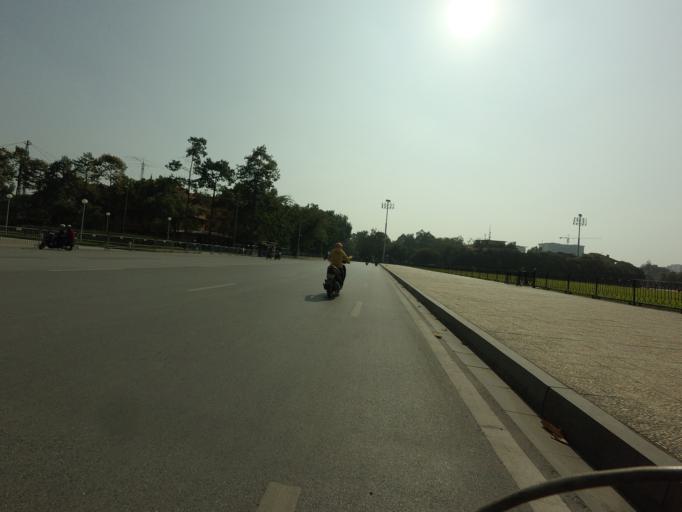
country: VN
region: Ha Noi
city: Hanoi
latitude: 21.0367
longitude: 105.8365
